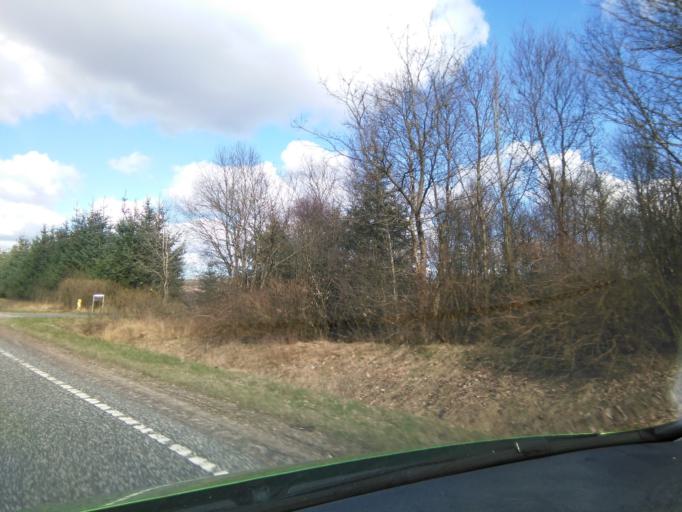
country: DK
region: Central Jutland
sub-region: Ikast-Brande Kommune
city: Bording Kirkeby
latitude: 56.1220
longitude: 9.3541
